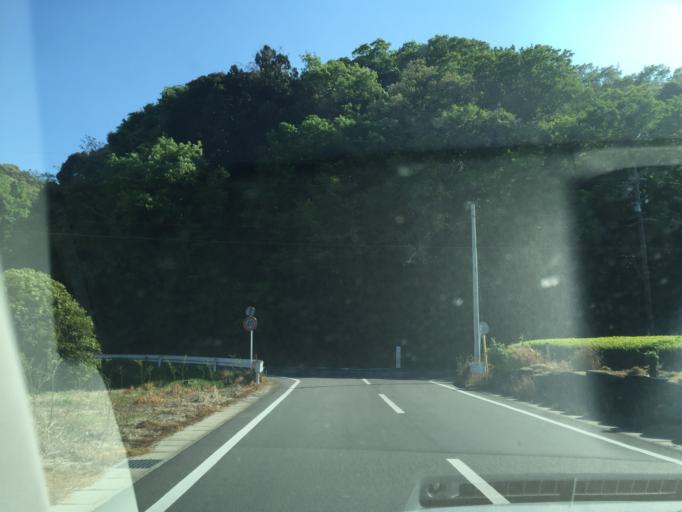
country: JP
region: Shizuoka
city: Kakegawa
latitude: 34.7712
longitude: 138.0511
